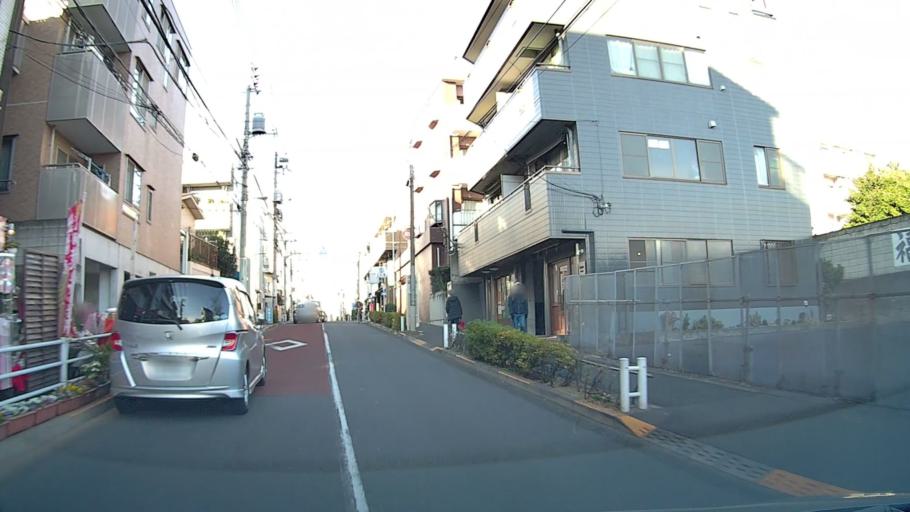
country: JP
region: Tokyo
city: Tokyo
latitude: 35.6947
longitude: 139.6742
